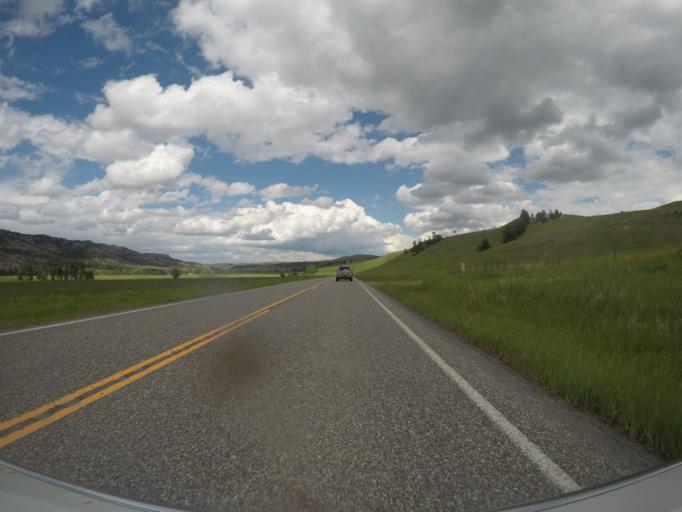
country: US
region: Montana
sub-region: Sweet Grass County
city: Big Timber
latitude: 45.6909
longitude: -110.0460
